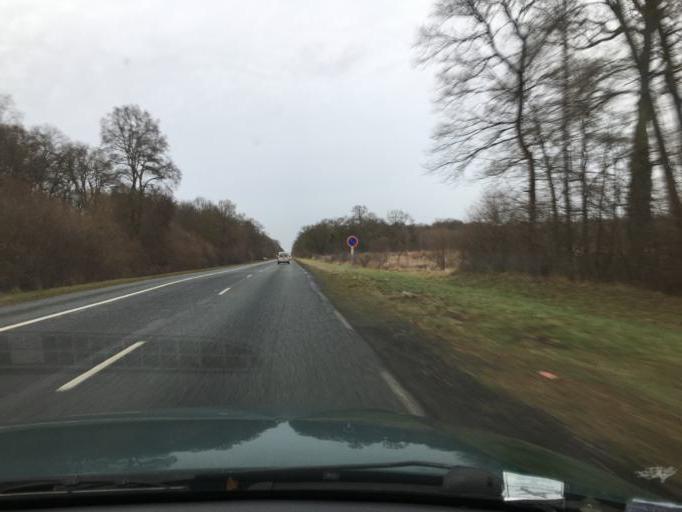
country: FR
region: Picardie
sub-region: Departement de l'Oise
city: Thiers-sur-Theve
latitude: 49.1612
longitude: 2.5534
